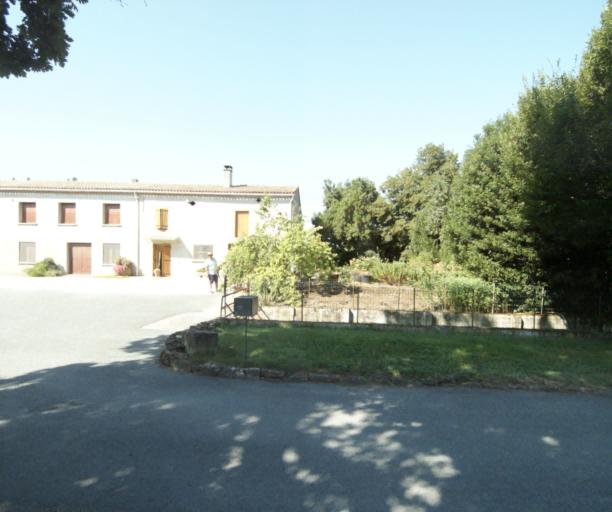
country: FR
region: Midi-Pyrenees
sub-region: Departement de la Haute-Garonne
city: Saint-Felix-Lauragais
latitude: 43.4281
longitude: 1.8369
